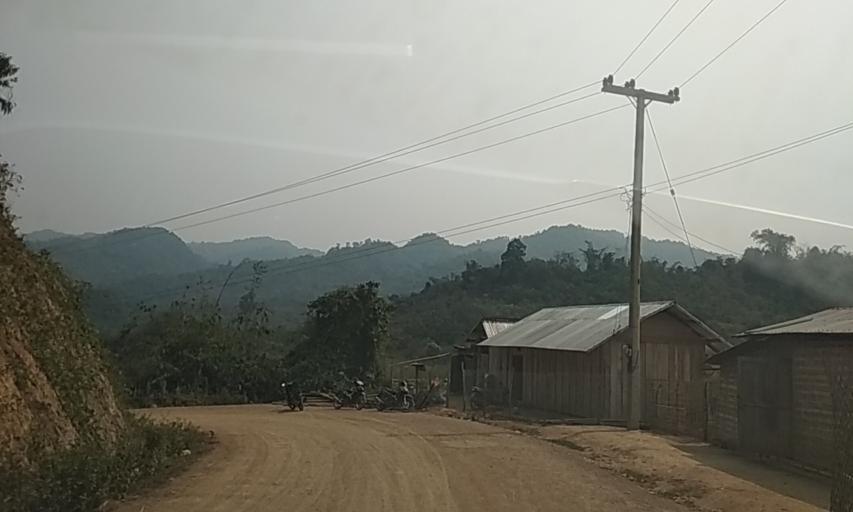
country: VN
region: Huyen Dien Bien
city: Dien Bien Phu
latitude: 21.4222
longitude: 102.7611
